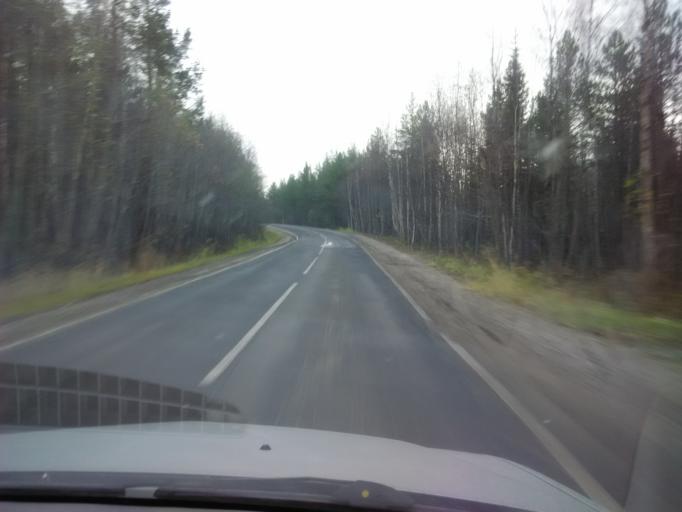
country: RU
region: Murmansk
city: Kandalaksha
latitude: 67.2479
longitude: 32.4245
